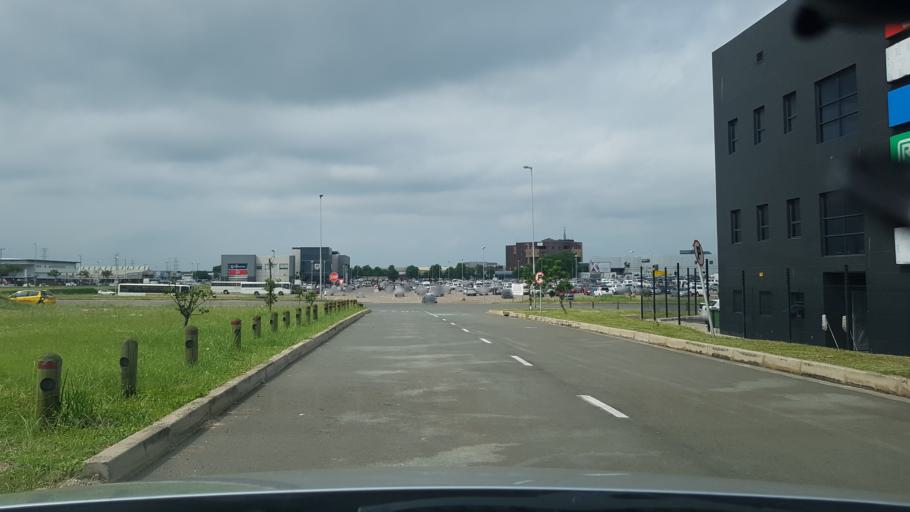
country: ZA
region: KwaZulu-Natal
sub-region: uThungulu District Municipality
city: Richards Bay
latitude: -28.7564
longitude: 32.0465
